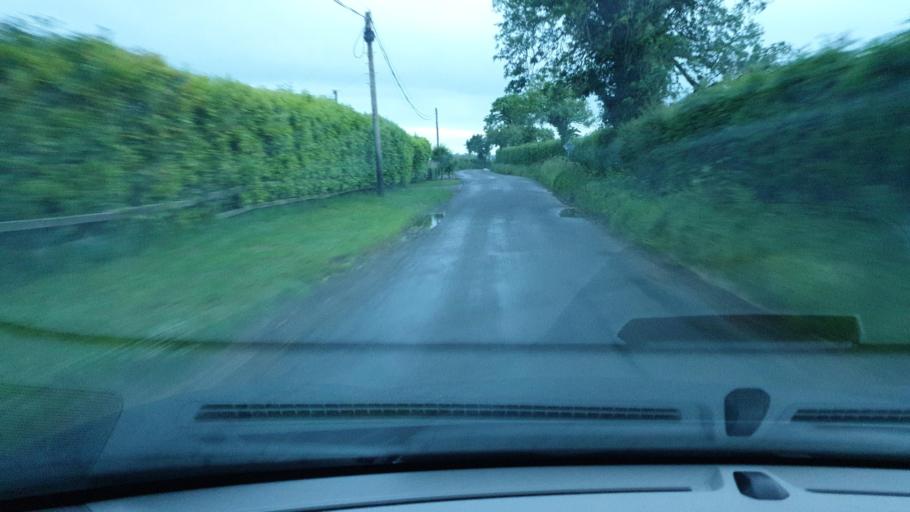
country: IE
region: Leinster
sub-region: An Mhi
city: Ashbourne
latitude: 53.5343
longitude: -6.3360
